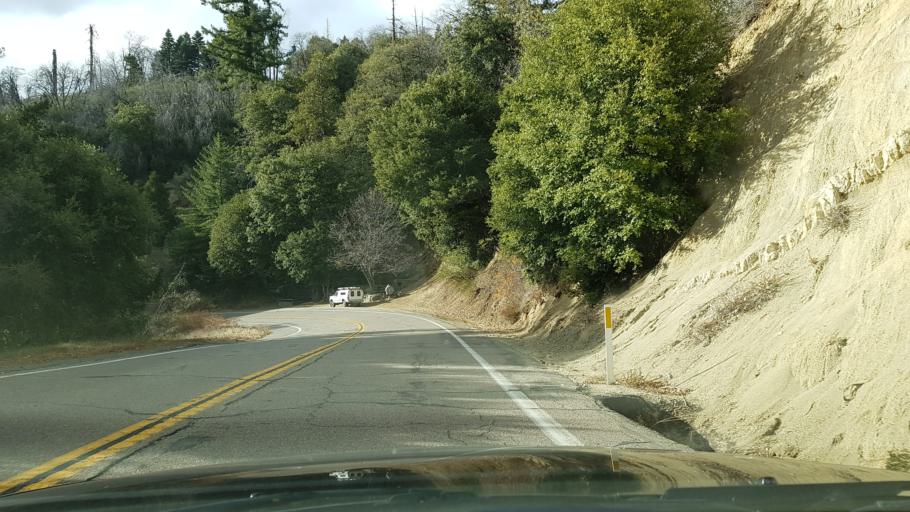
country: US
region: California
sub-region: Riverside County
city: Aguanga
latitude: 33.3141
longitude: -116.8697
